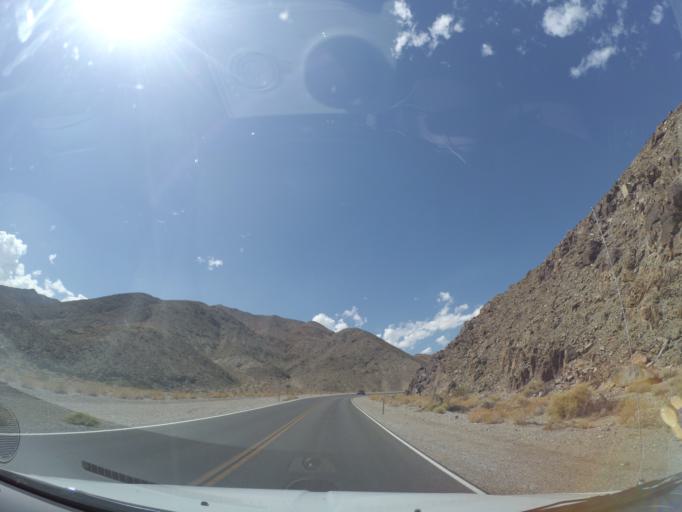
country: US
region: California
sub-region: San Bernardino County
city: Searles Valley
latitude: 36.3356
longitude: -117.4767
